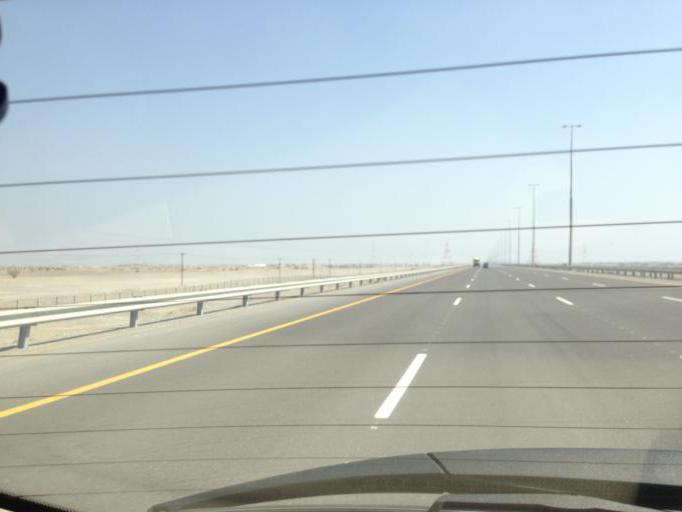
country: OM
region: Al Batinah
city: Barka'
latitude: 23.6036
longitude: 57.8207
